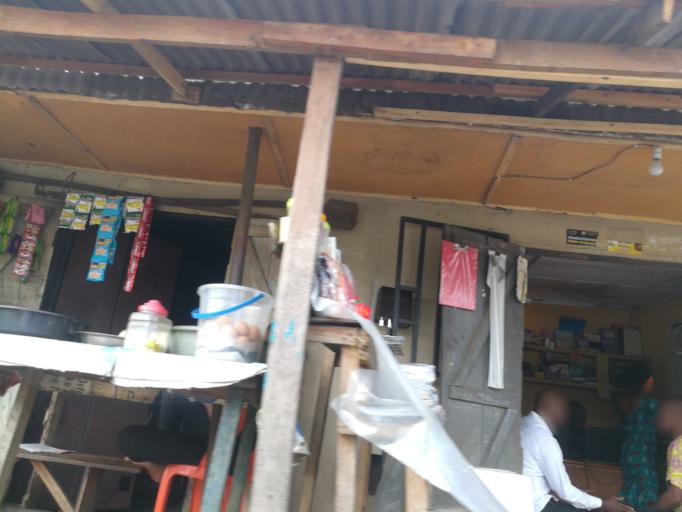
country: NG
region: Rivers
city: Okrika
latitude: 4.7565
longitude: 7.0987
